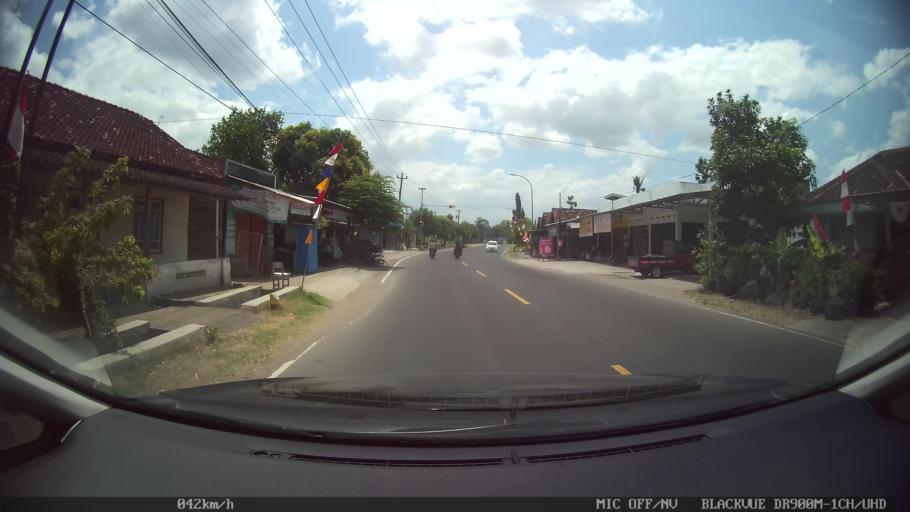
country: ID
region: Daerah Istimewa Yogyakarta
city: Bantul
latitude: -7.9062
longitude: 110.3447
